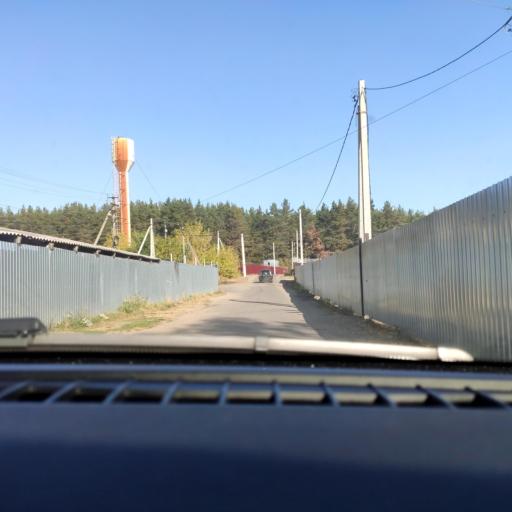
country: RU
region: Voronezj
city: Maslovka
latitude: 51.5448
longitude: 39.2193
